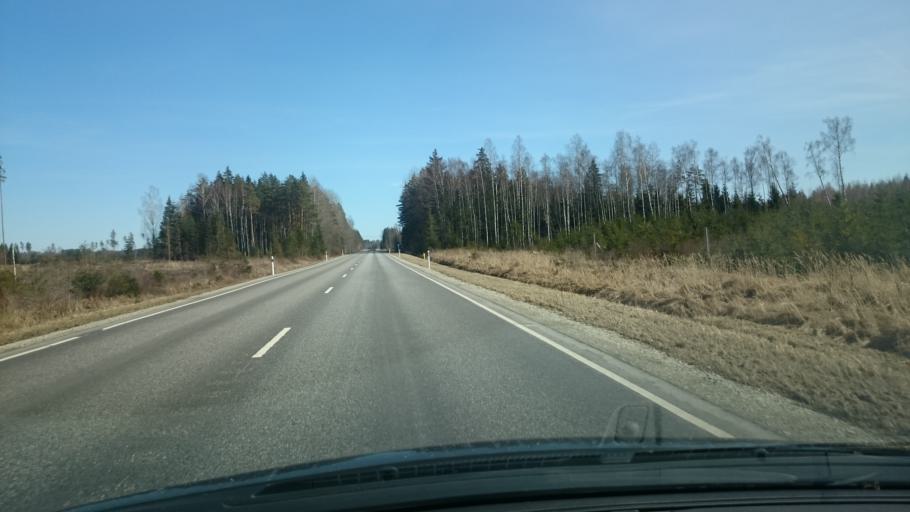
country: EE
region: Paernumaa
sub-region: Vaendra vald (alev)
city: Vandra
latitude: 58.6673
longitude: 25.1661
